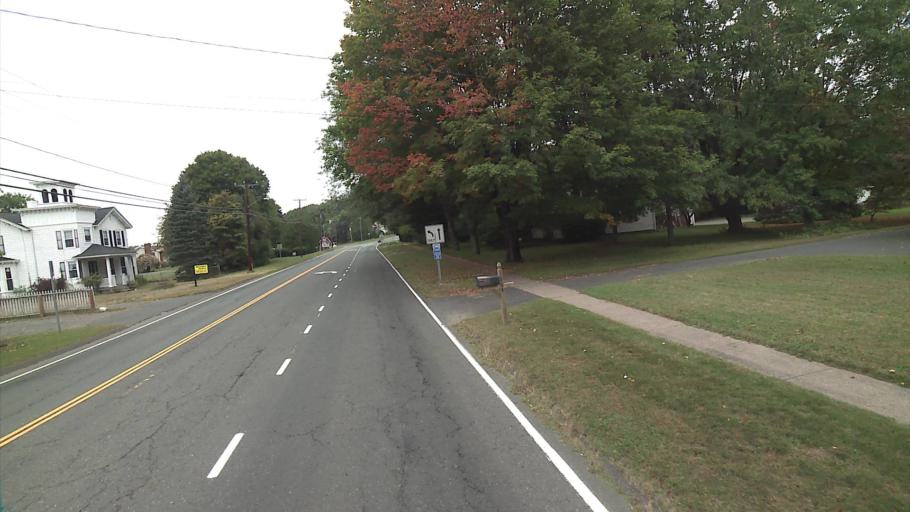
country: US
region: Connecticut
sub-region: Hartford County
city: Windsor Locks
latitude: 41.9075
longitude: -72.6791
